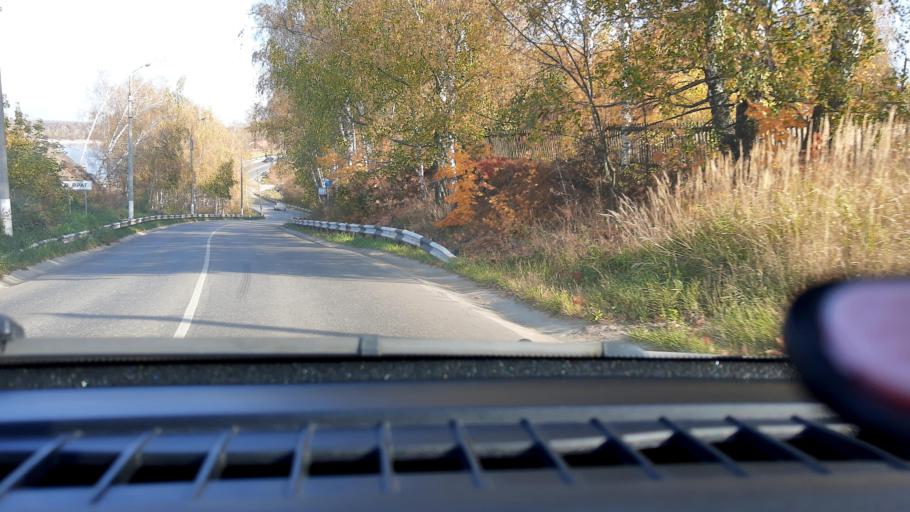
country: RU
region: Nizjnij Novgorod
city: Kstovo
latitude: 56.1557
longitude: 44.2440
